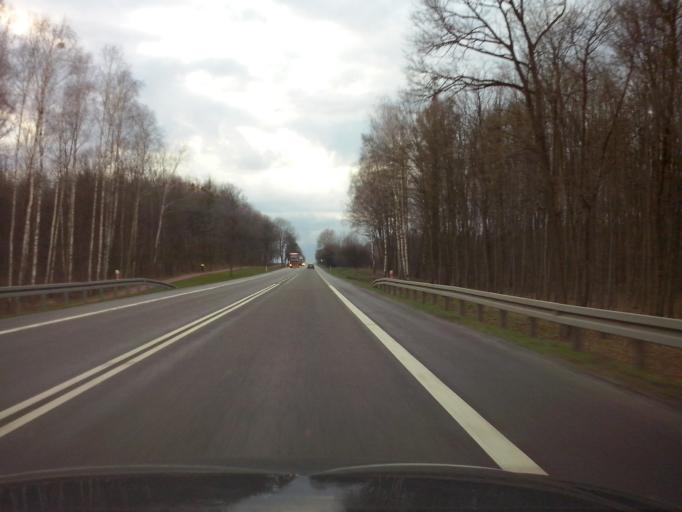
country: PL
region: Lublin Voivodeship
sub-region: Chelm
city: Chelm
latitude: 51.1563
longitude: 23.4068
